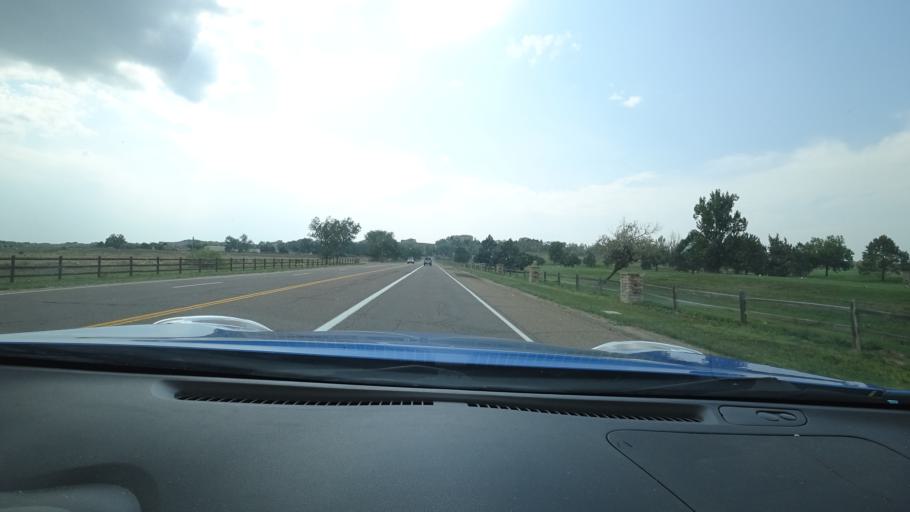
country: US
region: Colorado
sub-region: Adams County
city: Todd Creek
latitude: 39.9253
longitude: -104.8784
